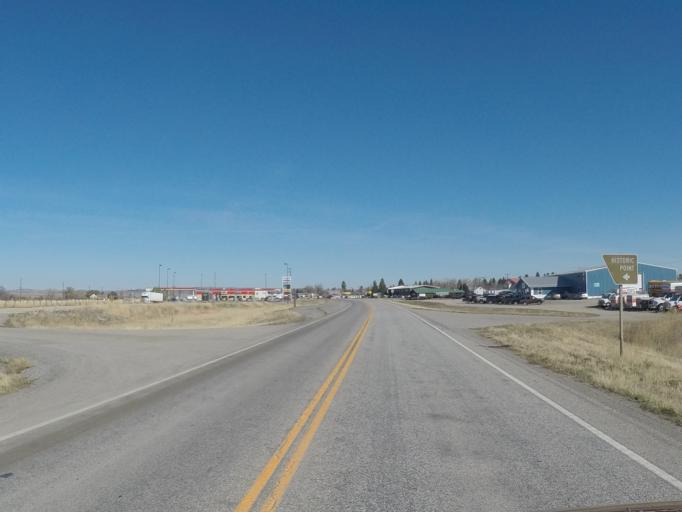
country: US
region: Montana
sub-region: Sweet Grass County
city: Big Timber
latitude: 45.8303
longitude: -109.9648
